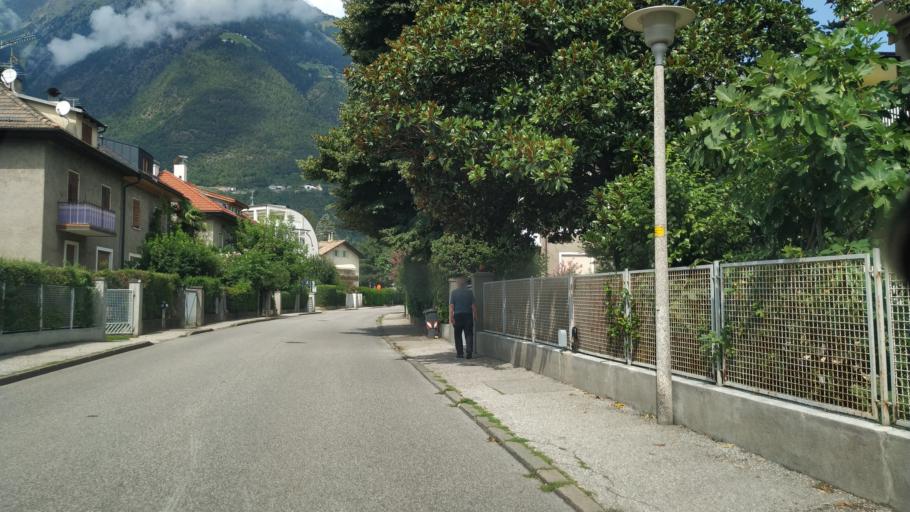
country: IT
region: Trentino-Alto Adige
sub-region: Bolzano
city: Merano
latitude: 46.6773
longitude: 11.1483
